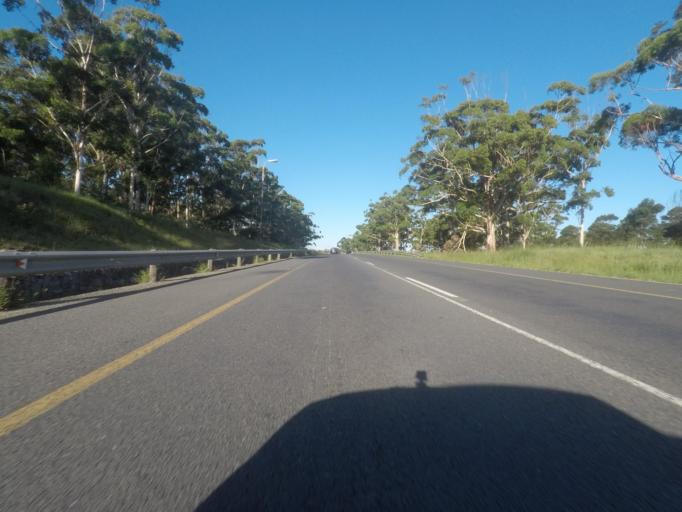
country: ZA
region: Eastern Cape
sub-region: Buffalo City Metropolitan Municipality
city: East London
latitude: -33.0462
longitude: 27.8239
